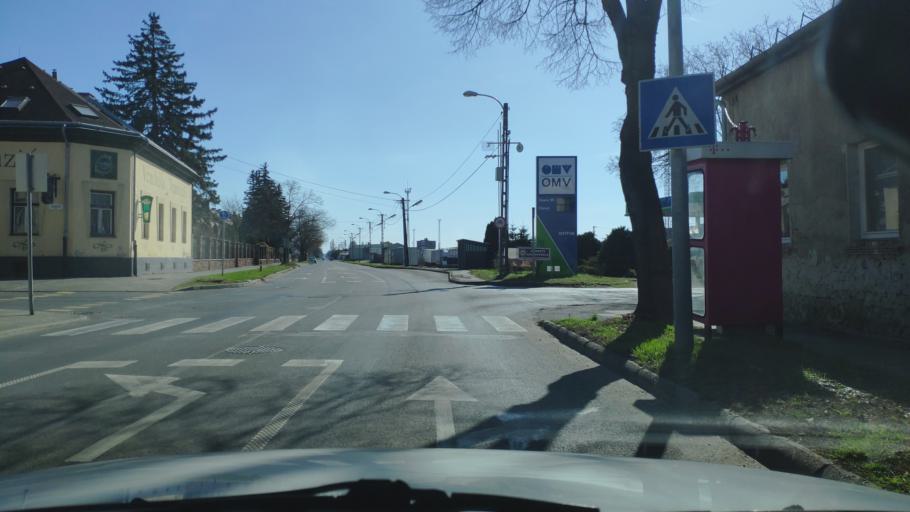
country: HU
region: Zala
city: Nagykanizsa
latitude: 46.4441
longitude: 16.9897
